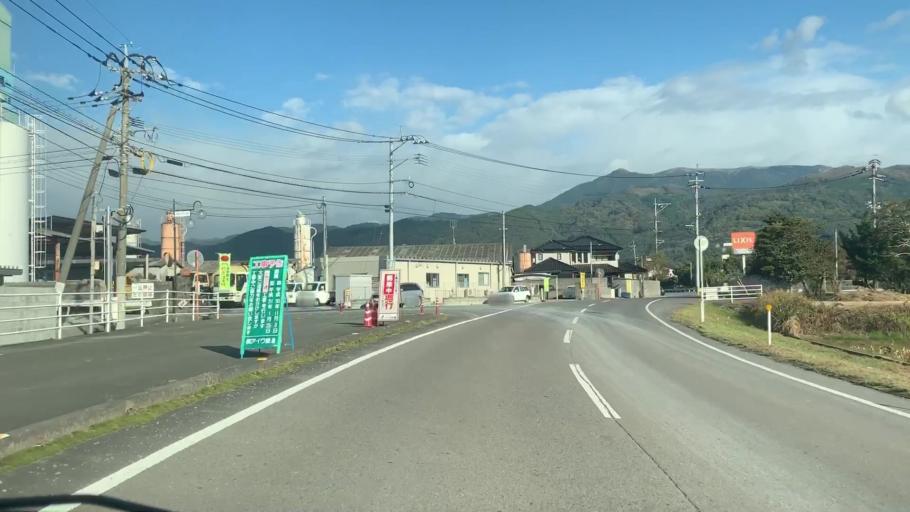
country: JP
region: Saga Prefecture
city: Takeocho-takeo
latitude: 33.2783
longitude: 130.1446
